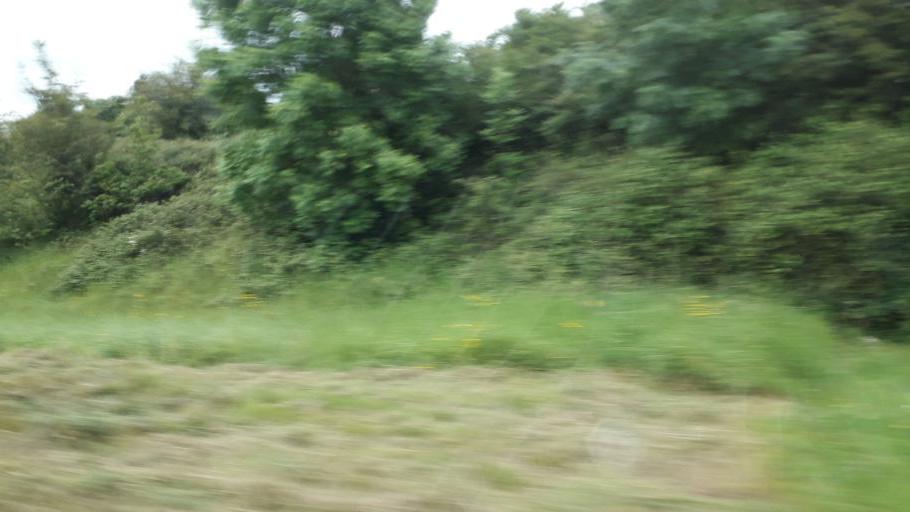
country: IE
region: Leinster
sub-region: County Carlow
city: Bagenalstown
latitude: 52.7353
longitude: -6.9869
